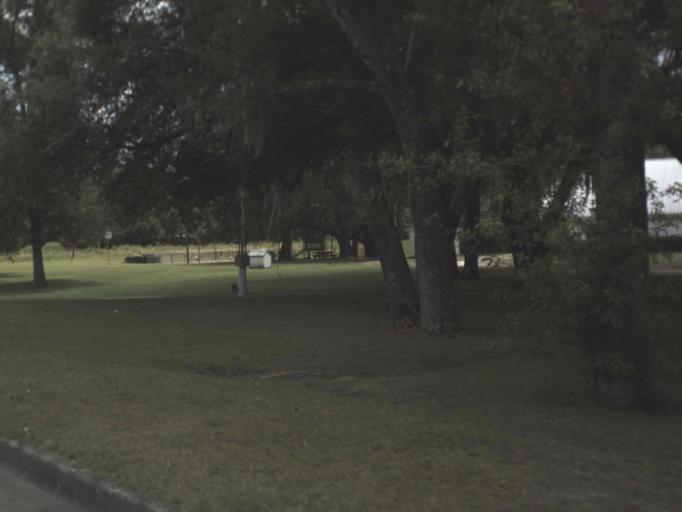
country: US
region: Florida
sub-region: Taylor County
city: Perry
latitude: 30.0903
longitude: -83.5356
